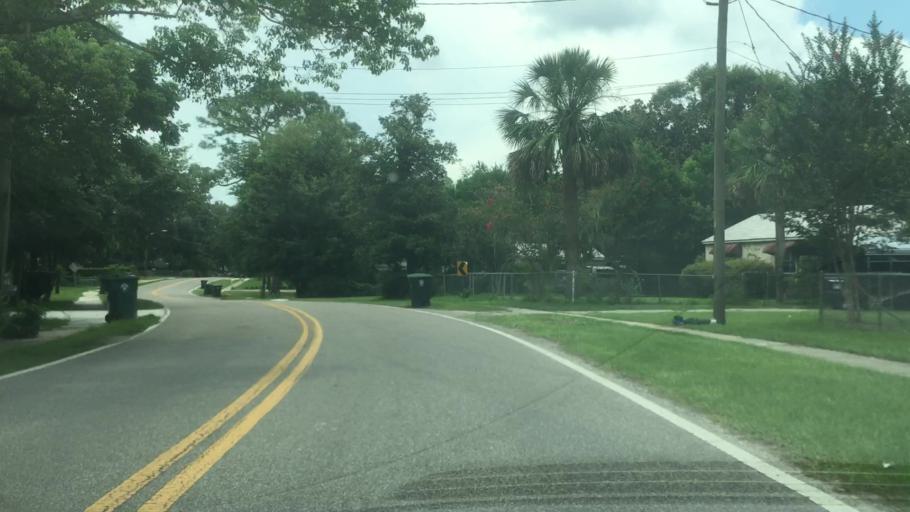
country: US
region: Florida
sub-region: Duval County
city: Jacksonville
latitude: 30.3041
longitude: -81.5494
